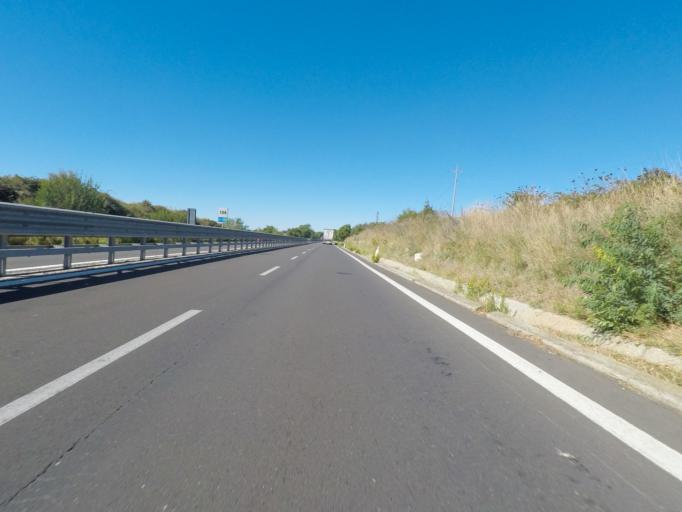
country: IT
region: Latium
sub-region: Provincia di Viterbo
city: Montalto di Castro
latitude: 42.3324
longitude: 11.6272
